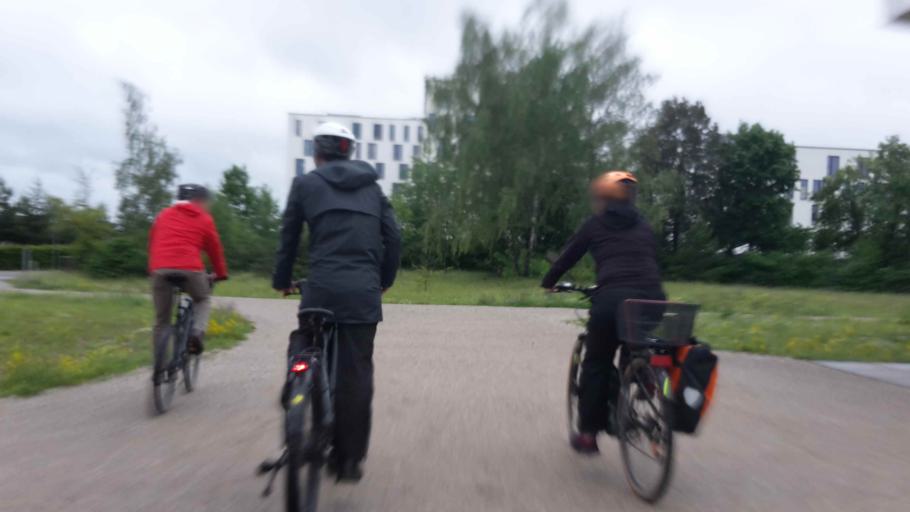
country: DE
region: Bavaria
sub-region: Upper Bavaria
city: Unterfoehring
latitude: 48.2112
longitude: 11.6152
